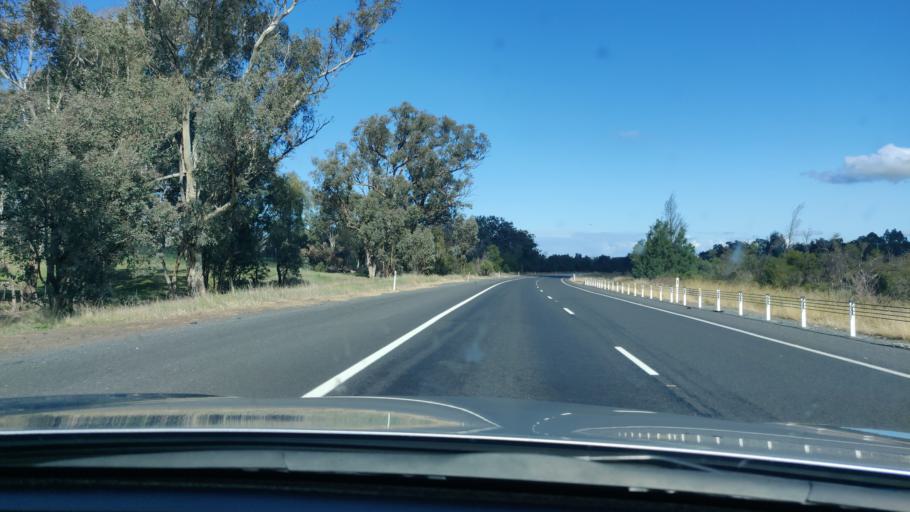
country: AU
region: New South Wales
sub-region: Greater Hume Shire
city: Holbrook
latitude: -35.8893
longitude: 147.1732
